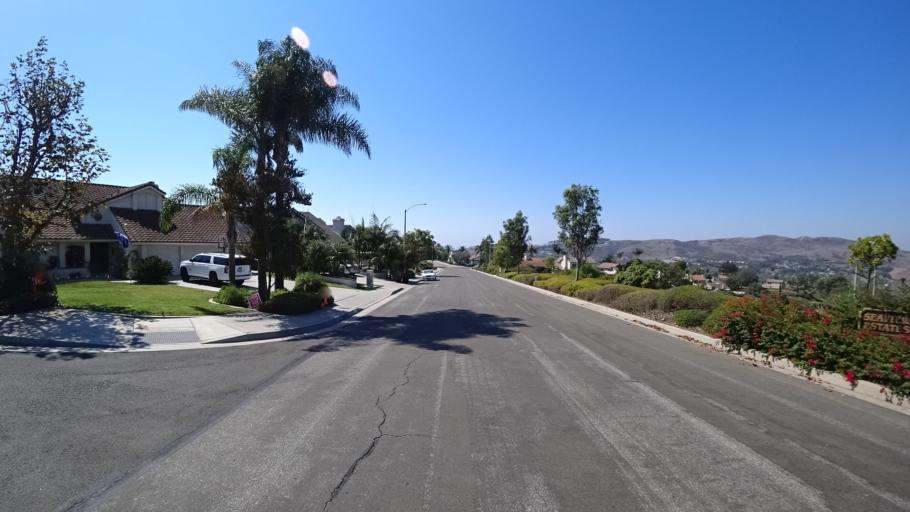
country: US
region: California
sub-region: Orange County
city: San Clemente
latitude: 33.4603
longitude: -117.6261
